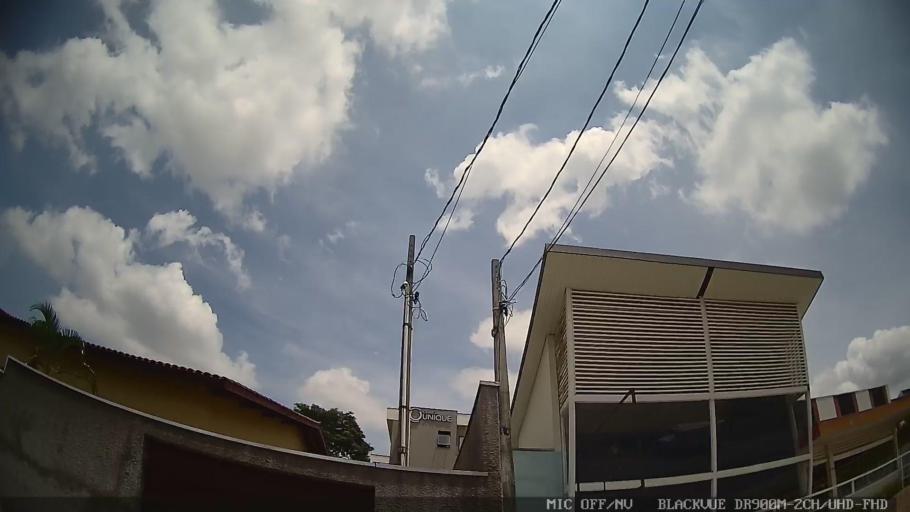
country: BR
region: Sao Paulo
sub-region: Vinhedo
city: Vinhedo
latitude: -23.0352
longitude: -46.9797
